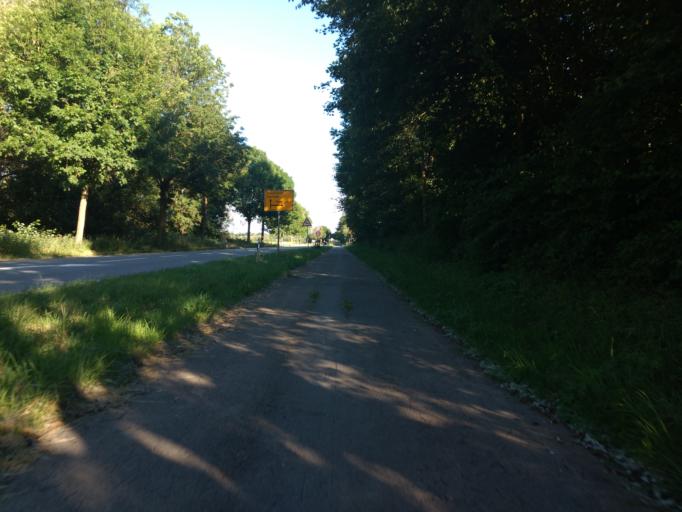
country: DE
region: Saarland
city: Rehlingen-Siersburg
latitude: 49.3983
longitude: 6.6580
